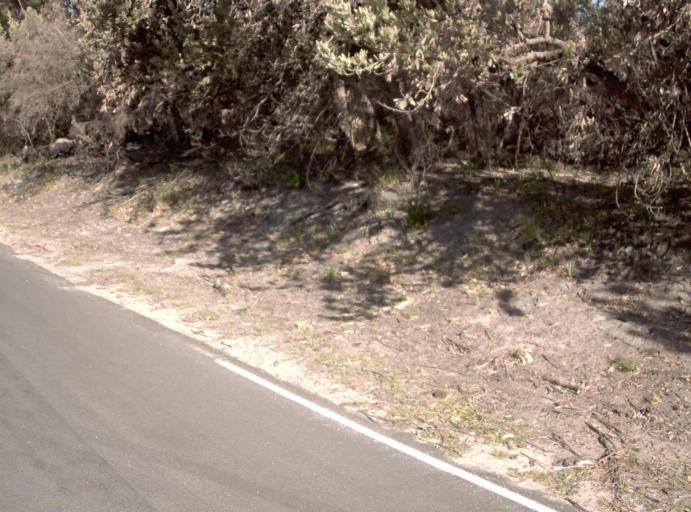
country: AU
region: Victoria
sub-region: East Gippsland
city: Lakes Entrance
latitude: -37.7989
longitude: 148.7372
